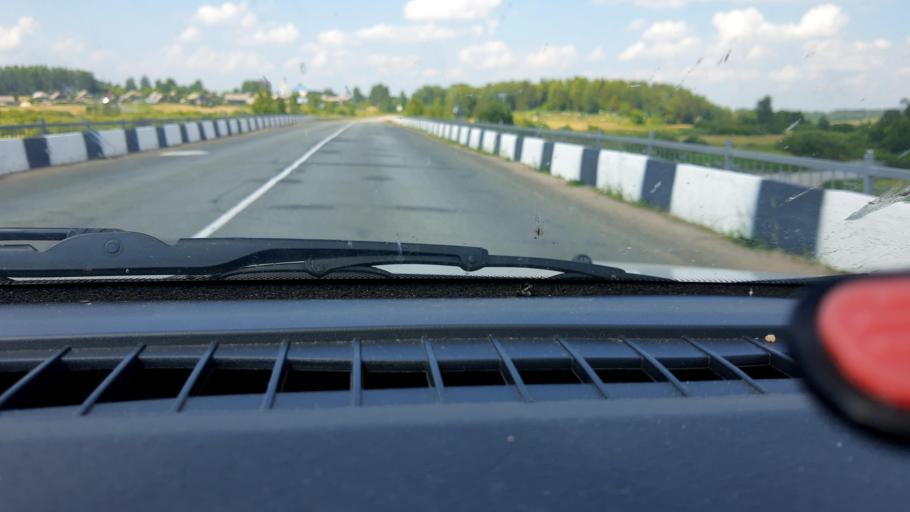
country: RU
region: Nizjnij Novgorod
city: Tonkino
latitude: 57.2622
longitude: 46.4591
